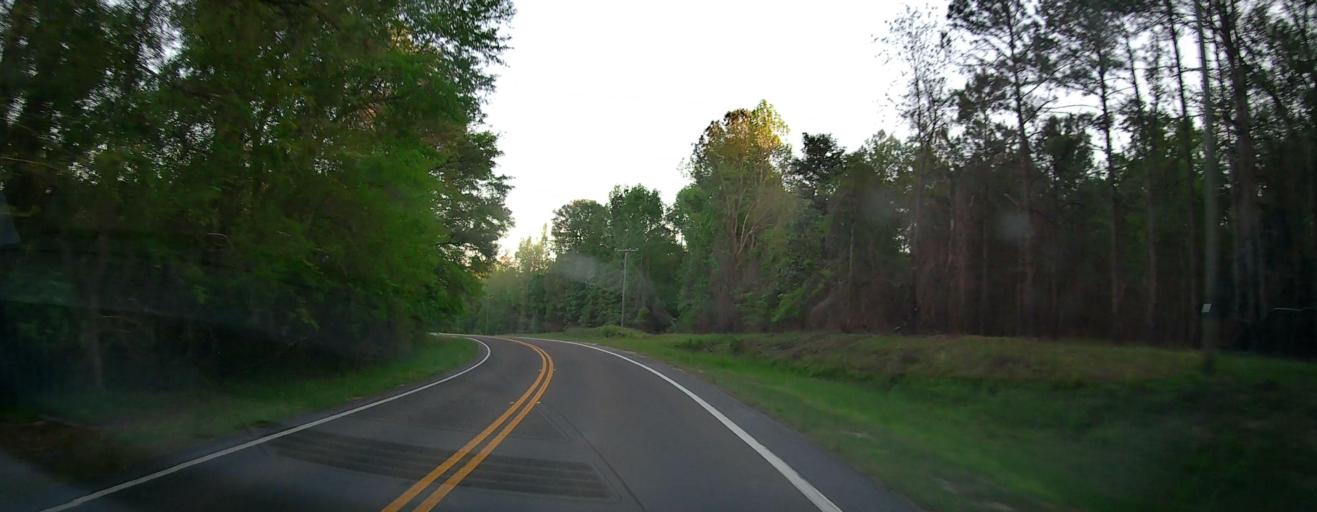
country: US
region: Georgia
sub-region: Talbot County
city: Talbotton
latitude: 32.5250
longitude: -84.6067
